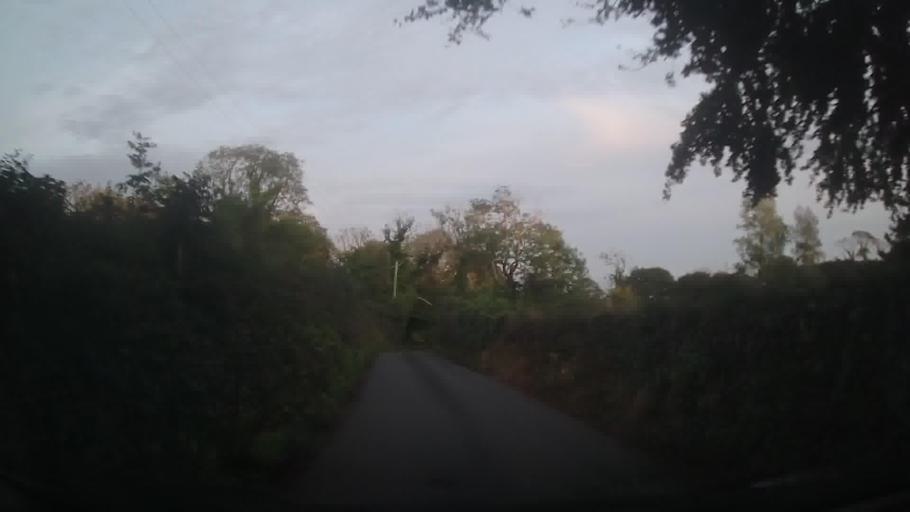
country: GB
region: Wales
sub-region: Pembrokeshire
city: Saundersfoot
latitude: 51.7397
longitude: -4.6615
